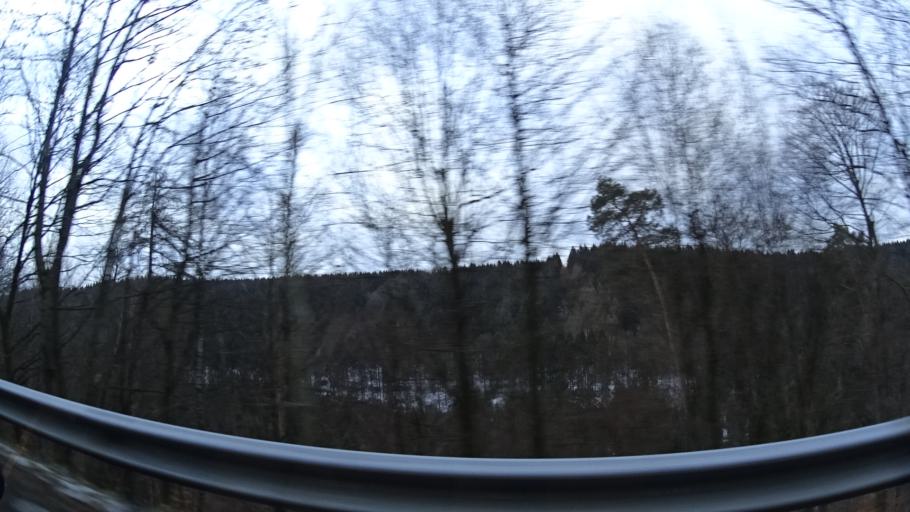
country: DE
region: Baden-Wuerttemberg
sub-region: Karlsruhe Region
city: Zwingenberg
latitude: 49.4495
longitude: 9.0333
